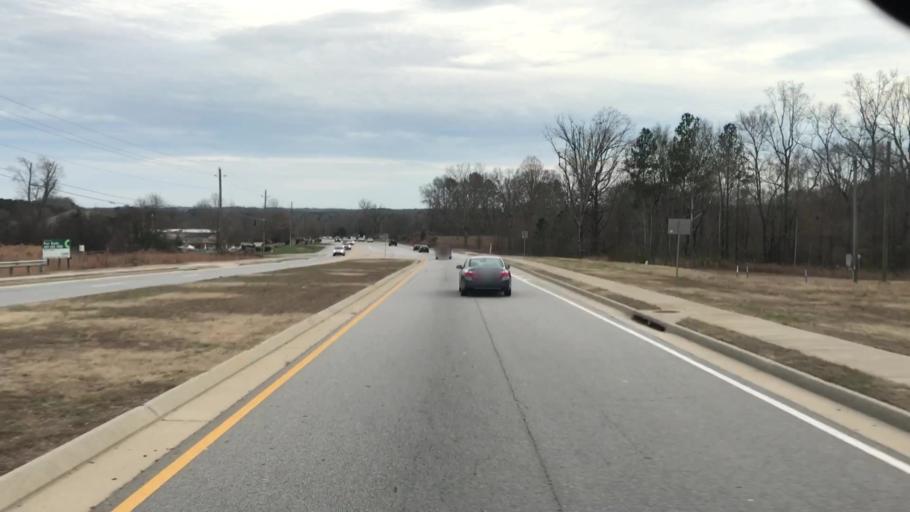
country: US
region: Georgia
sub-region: Jackson County
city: Hoschton
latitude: 34.0921
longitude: -83.8082
